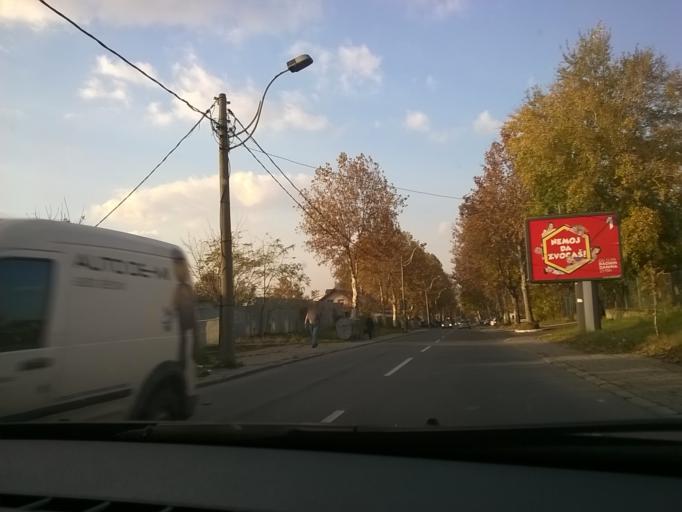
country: RS
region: Central Serbia
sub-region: Belgrade
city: Palilula
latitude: 44.8118
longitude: 20.4929
